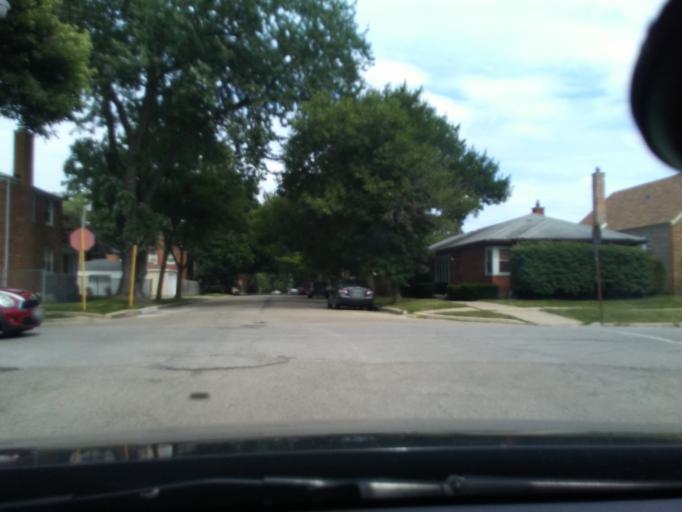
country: US
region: Illinois
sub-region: Cook County
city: Harwood Heights
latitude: 41.9738
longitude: -87.7953
